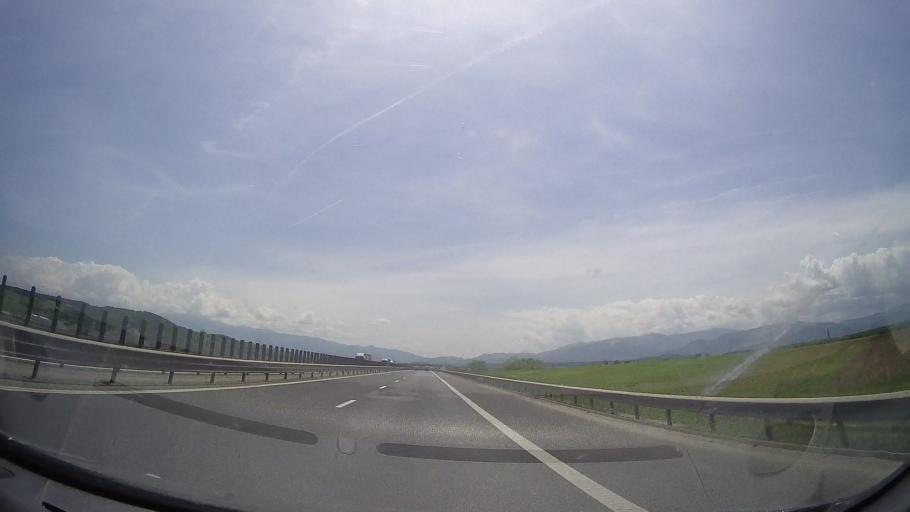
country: RO
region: Sibiu
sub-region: Comuna Selimbar
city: Selimbar
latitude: 45.7759
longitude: 24.2034
